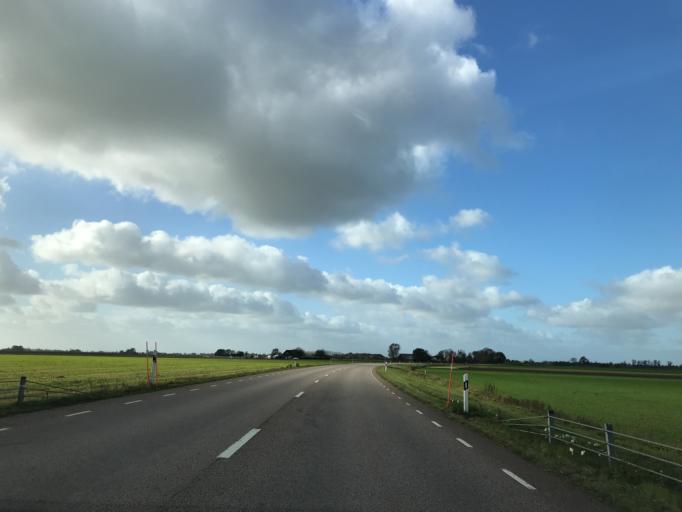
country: SE
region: Skane
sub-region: Helsingborg
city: Morarp
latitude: 56.0094
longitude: 12.9033
